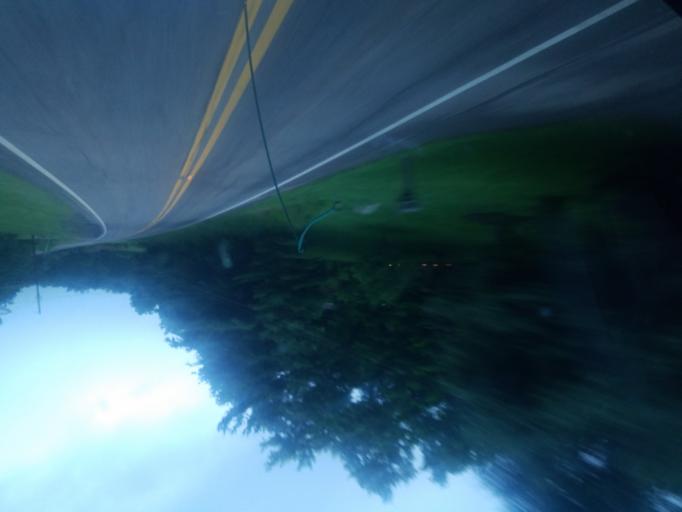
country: US
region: Ohio
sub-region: Carroll County
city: Carrollton
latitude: 40.5910
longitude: -81.0262
